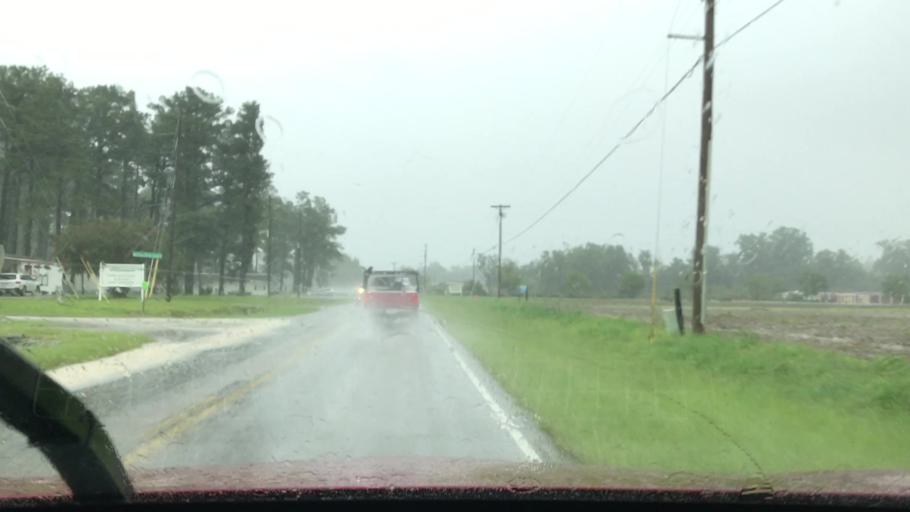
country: US
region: South Carolina
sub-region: Horry County
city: Red Hill
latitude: 33.8625
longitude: -78.9924
